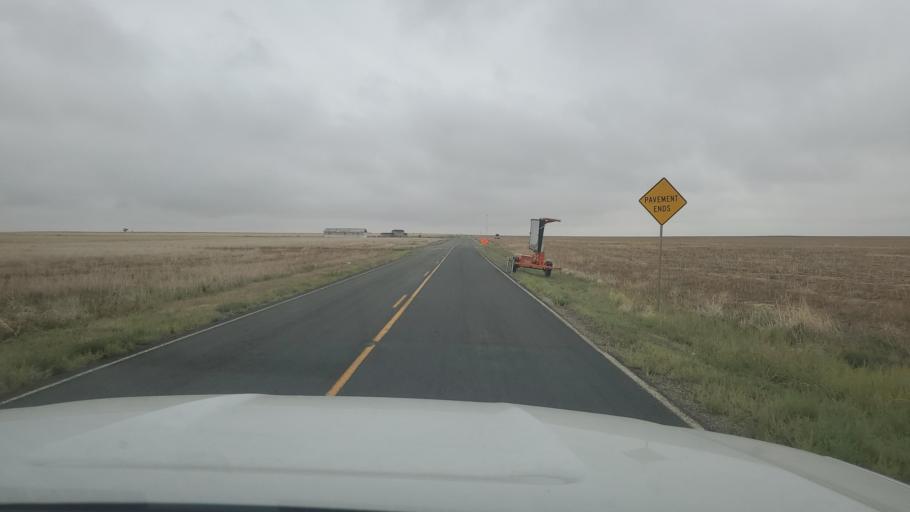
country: US
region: Colorado
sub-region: Weld County
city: Lochbuie
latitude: 39.9426
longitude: -104.6029
